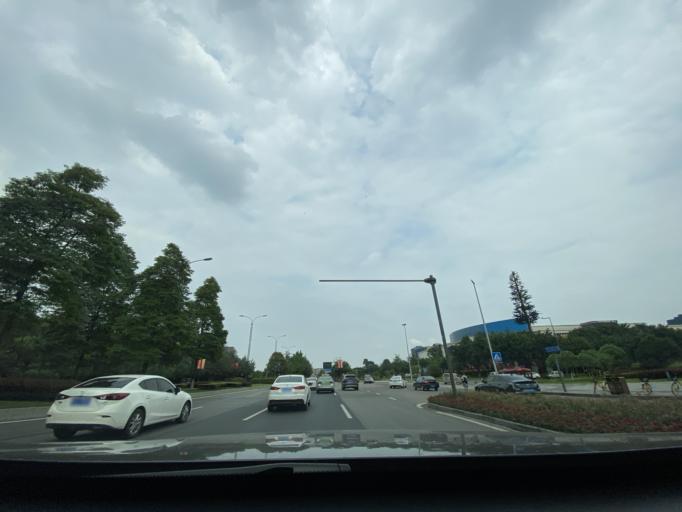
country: CN
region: Sichuan
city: Dongsheng
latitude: 30.6055
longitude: 103.9339
